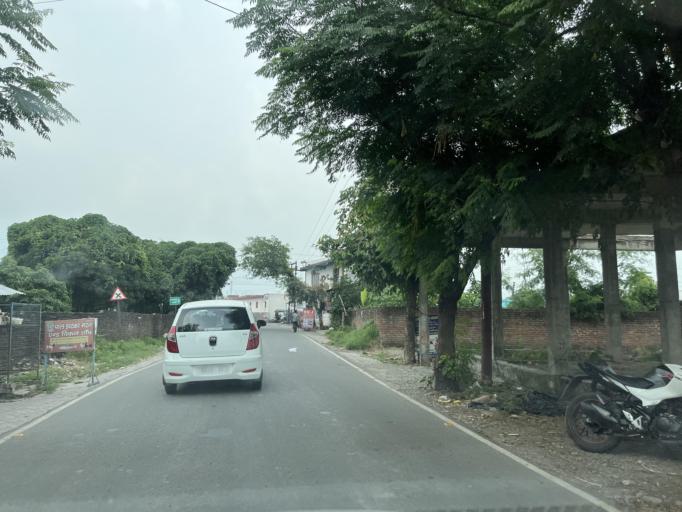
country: IN
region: Uttarakhand
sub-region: Naini Tal
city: Haldwani
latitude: 29.1968
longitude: 79.4856
